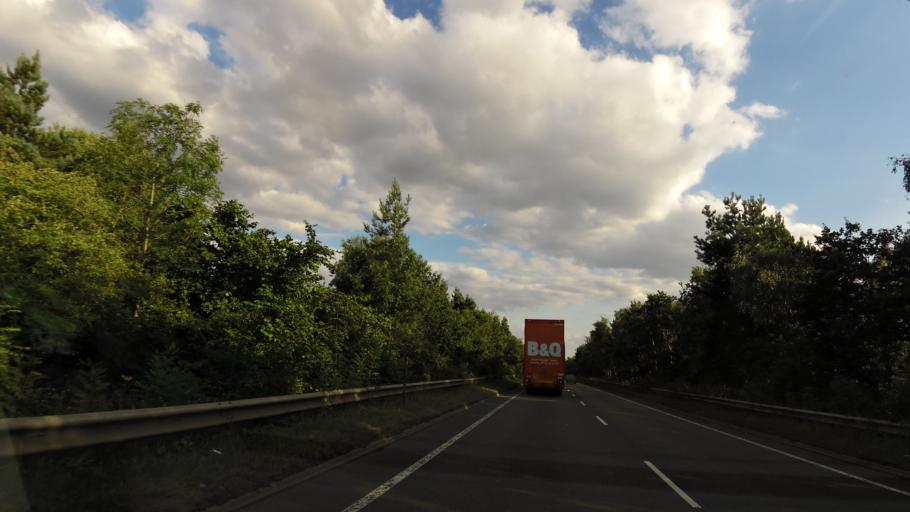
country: GB
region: England
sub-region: Rotherham
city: Woodsetts
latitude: 53.3202
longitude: -1.1532
